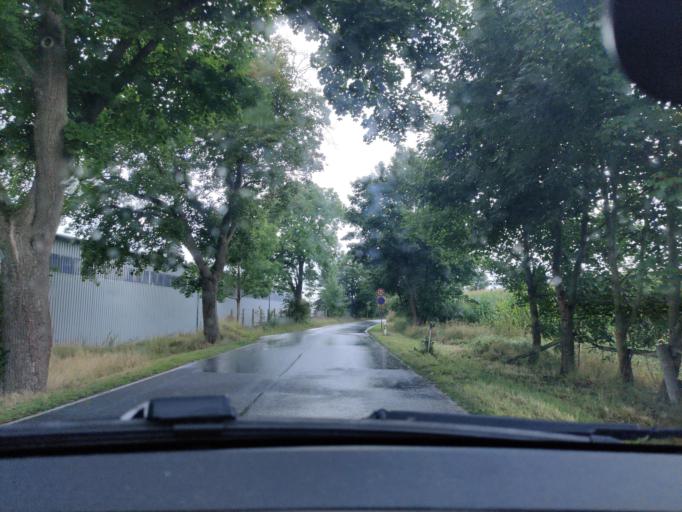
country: DE
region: Mecklenburg-Vorpommern
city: Wesenberg
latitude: 53.2763
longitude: 12.9890
